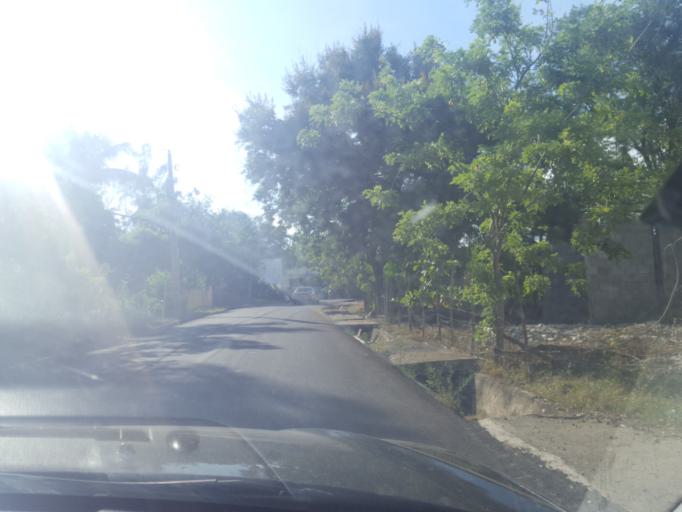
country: DO
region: La Vega
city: Rio Verde Arriba
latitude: 19.3481
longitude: -70.6255
